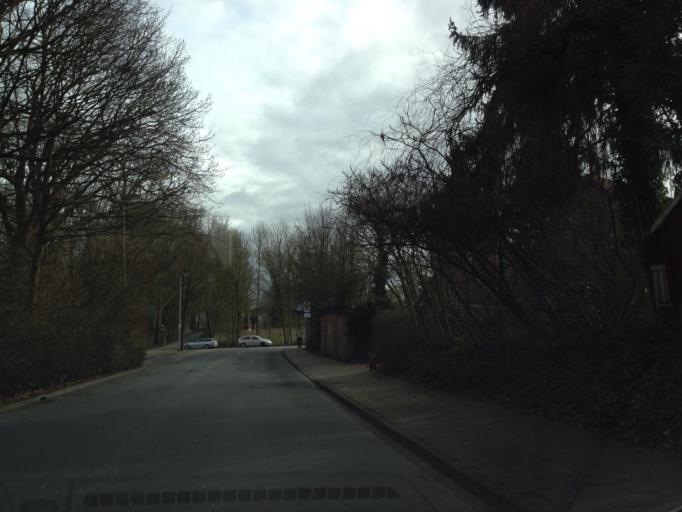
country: DE
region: North Rhine-Westphalia
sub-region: Regierungsbezirk Munster
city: Muenster
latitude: 51.9893
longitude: 7.5940
